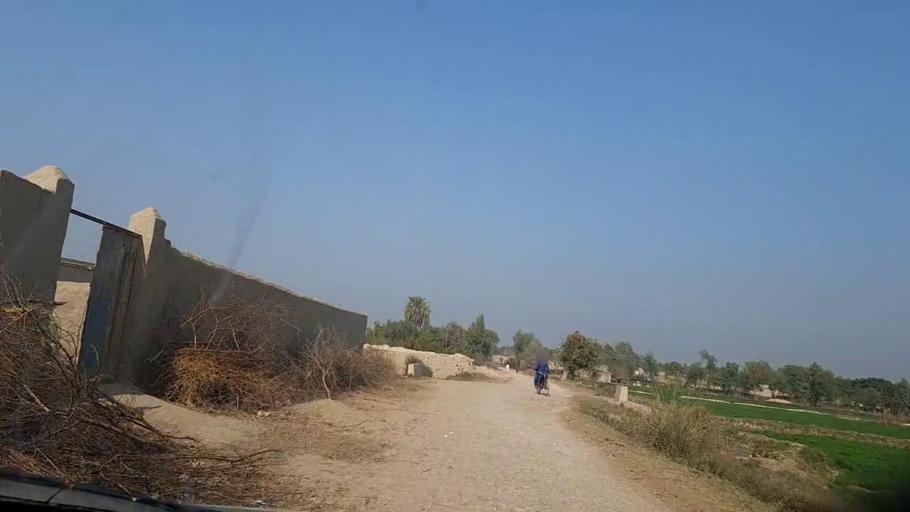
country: PK
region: Sindh
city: Moro
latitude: 26.8000
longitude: 67.9460
